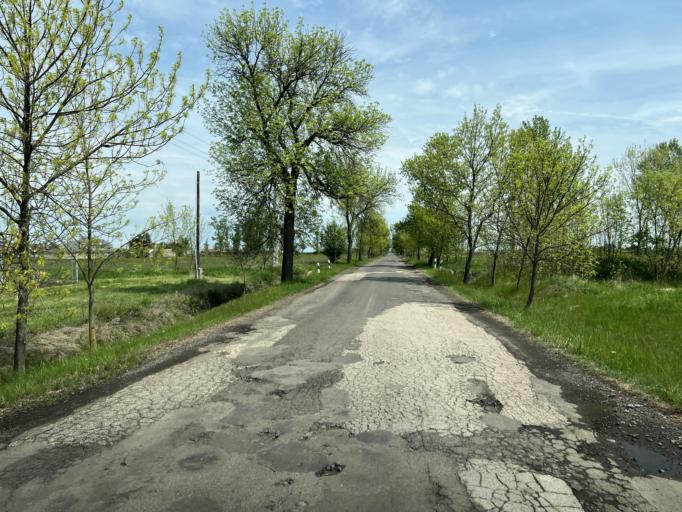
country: HU
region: Pest
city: Tapiogyorgye
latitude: 47.3481
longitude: 19.9517
